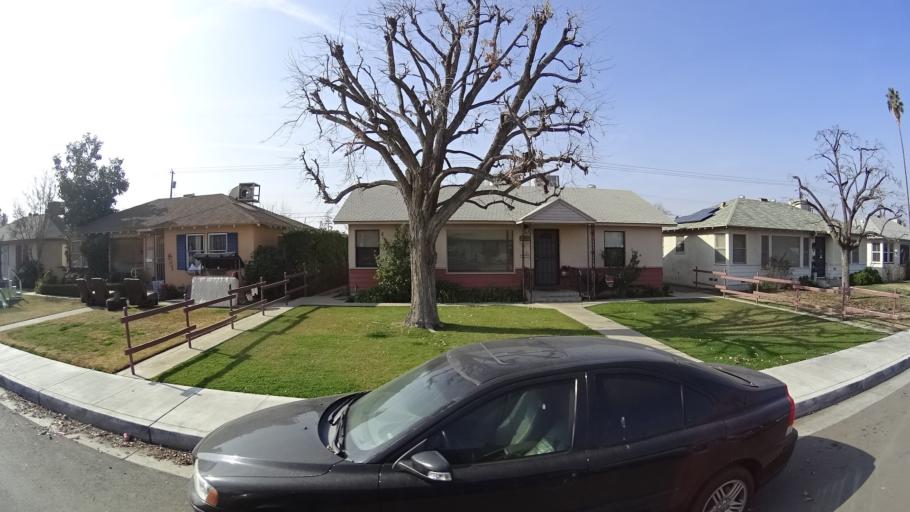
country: US
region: California
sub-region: Kern County
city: Bakersfield
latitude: 35.3555
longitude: -119.0350
